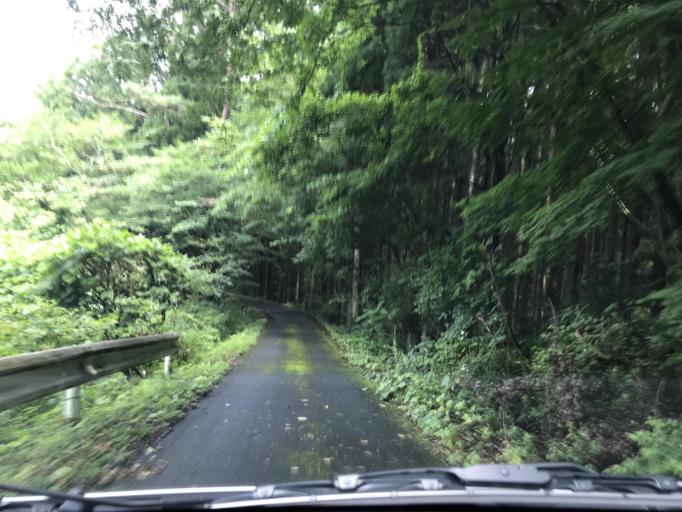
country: JP
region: Iwate
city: Mizusawa
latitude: 39.0589
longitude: 141.3837
